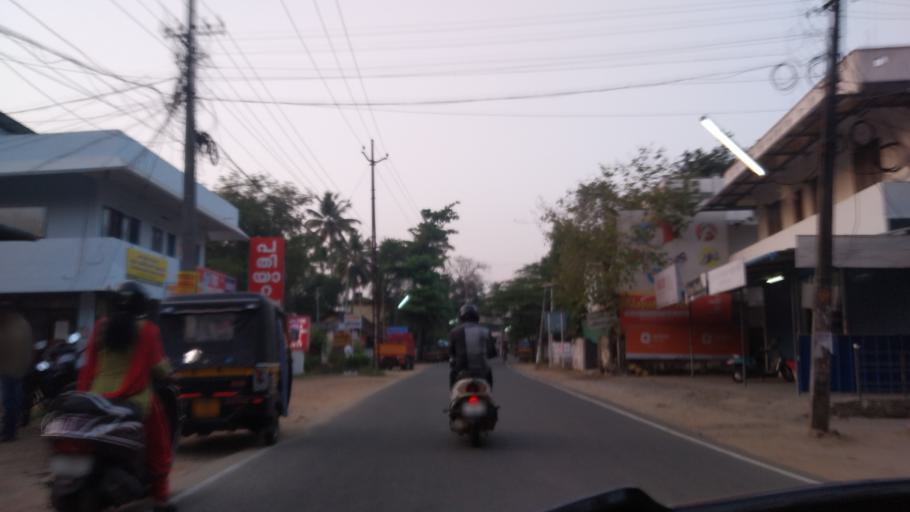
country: IN
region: Kerala
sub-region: Ernakulam
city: Elur
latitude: 10.1371
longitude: 76.2305
